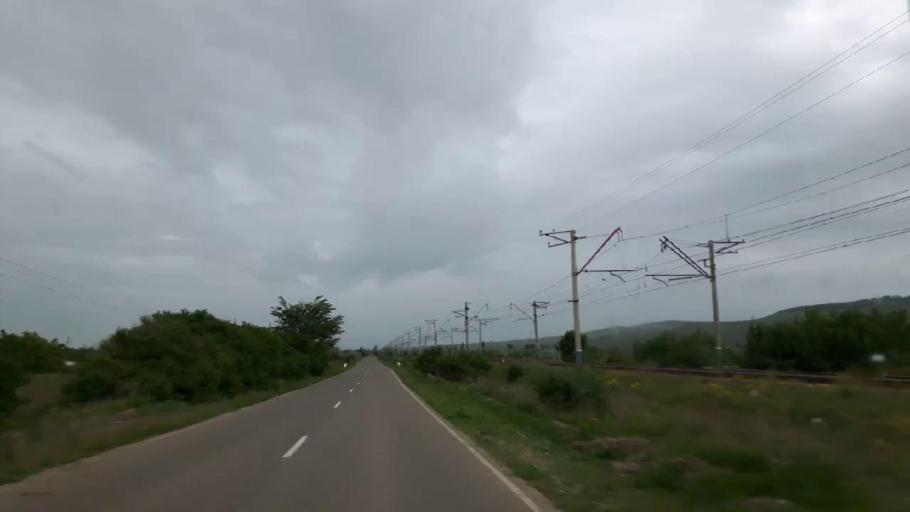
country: GE
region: Shida Kartli
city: Gori
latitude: 41.9959
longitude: 44.0231
